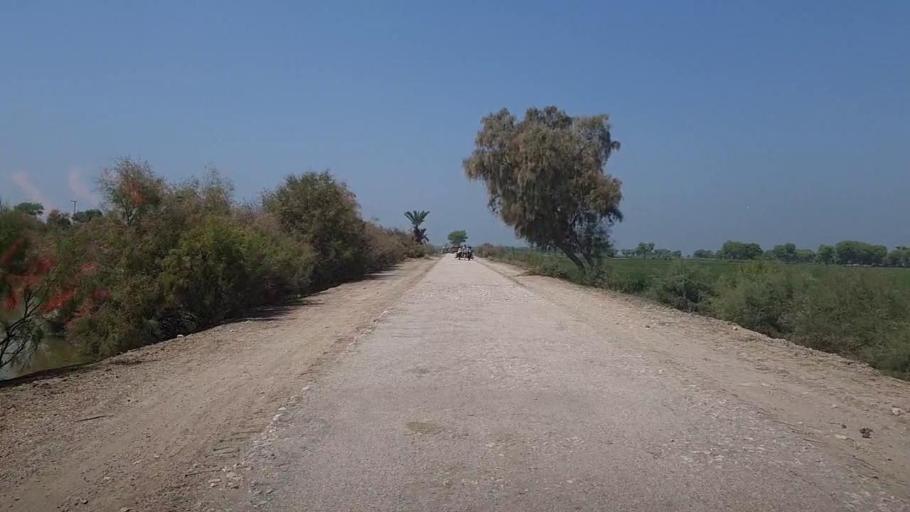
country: PK
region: Sindh
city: Kandhkot
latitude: 28.2948
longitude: 69.2953
